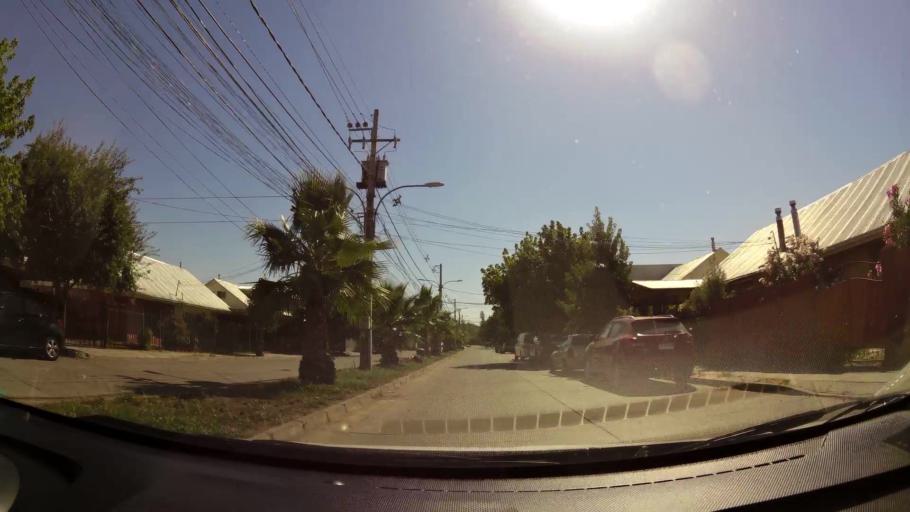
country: CL
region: Maule
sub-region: Provincia de Curico
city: Curico
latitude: -34.9700
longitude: -71.2560
